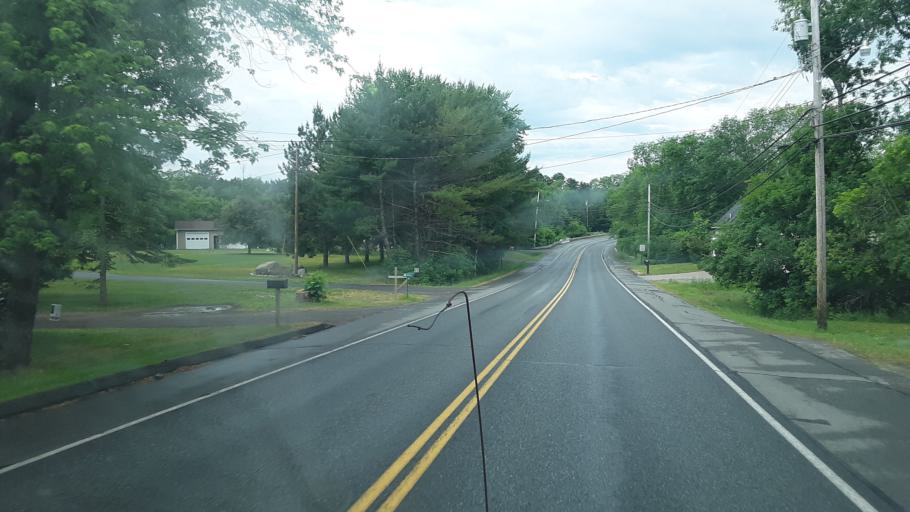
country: US
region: Maine
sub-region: Penobscot County
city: Eddington
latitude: 44.8182
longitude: -68.7053
